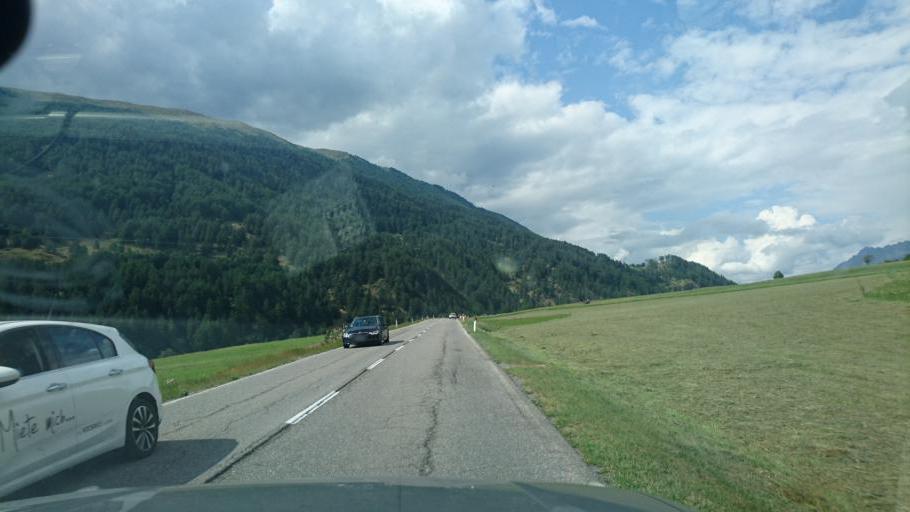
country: IT
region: Trentino-Alto Adige
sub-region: Bolzano
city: Malles Venosta
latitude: 46.7191
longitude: 10.5350
